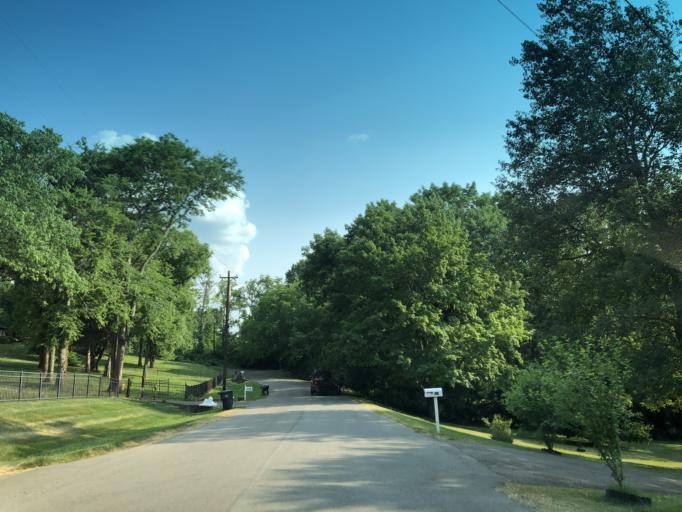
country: US
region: Tennessee
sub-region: Davidson County
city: Goodlettsville
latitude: 36.2703
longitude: -86.7328
